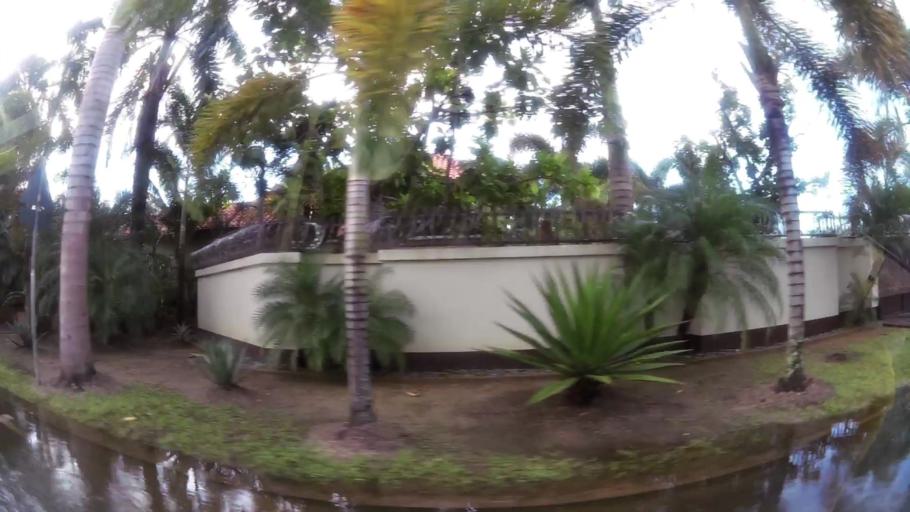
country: SR
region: Paramaribo
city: Paramaribo
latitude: 5.8377
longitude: -55.1871
